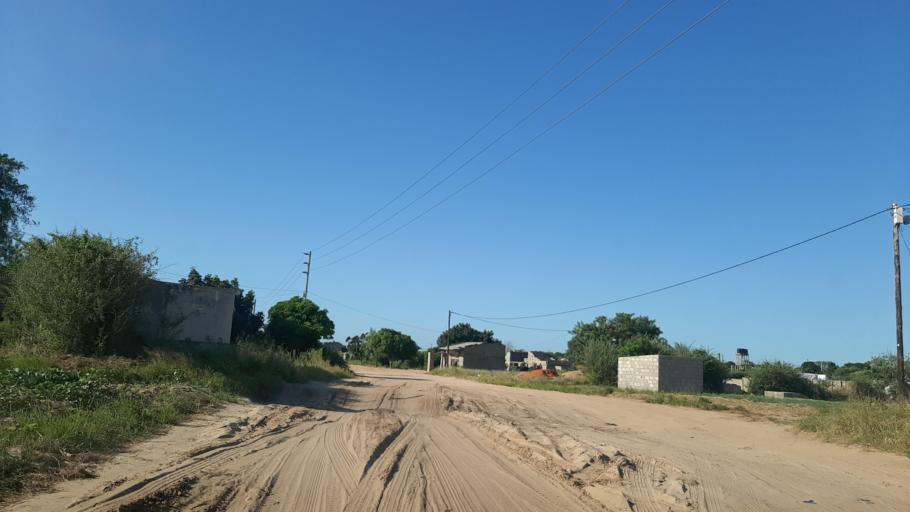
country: MZ
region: Maputo City
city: Maputo
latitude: -25.7587
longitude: 32.5502
